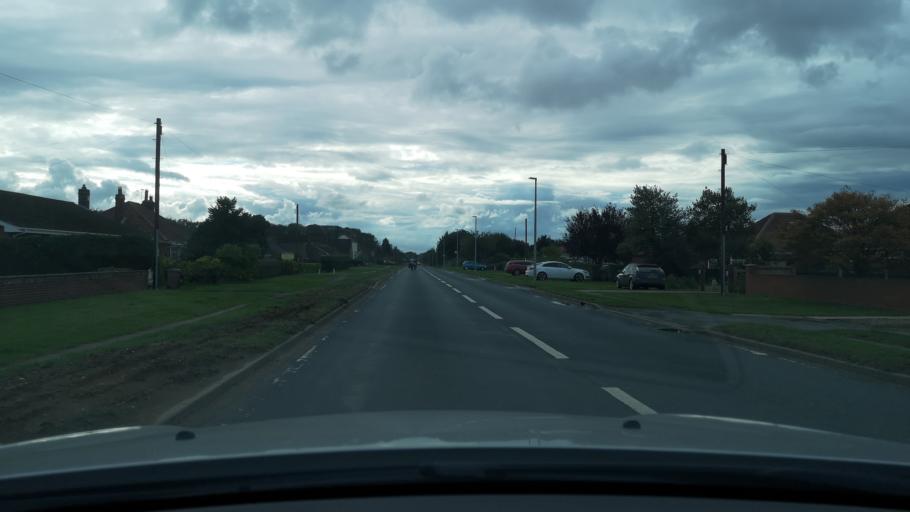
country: GB
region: England
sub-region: East Riding of Yorkshire
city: North Cave
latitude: 53.7781
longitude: -0.6564
